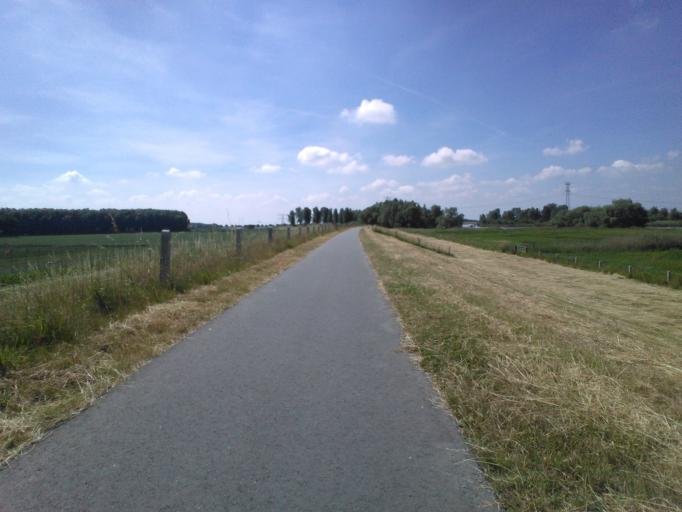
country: NL
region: North Brabant
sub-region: Gemeente Werkendam
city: Werkendam
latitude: 51.7699
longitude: 4.8633
